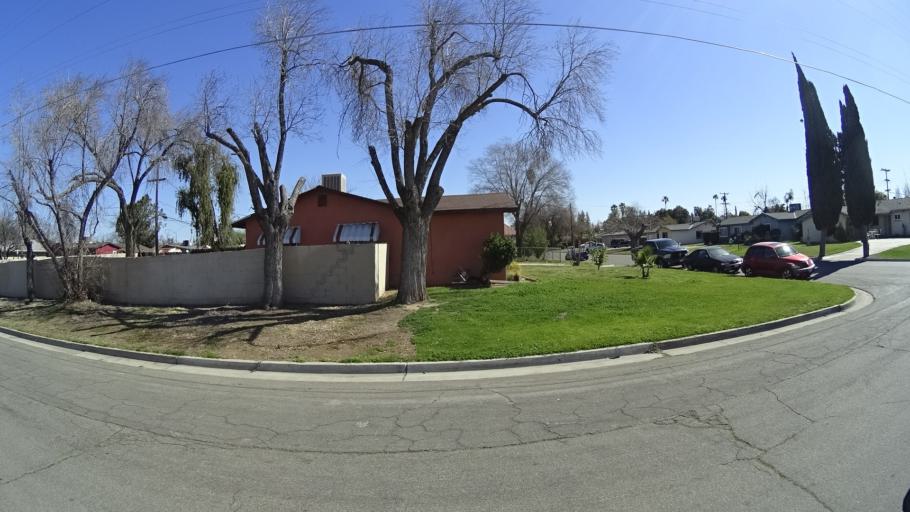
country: US
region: California
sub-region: Fresno County
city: Clovis
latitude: 36.8368
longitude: -119.7880
